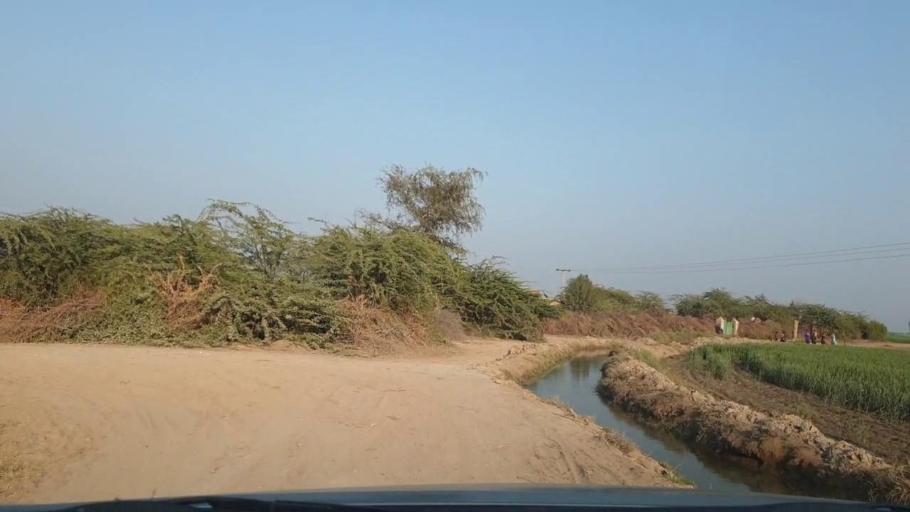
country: PK
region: Sindh
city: Tando Adam
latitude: 25.6868
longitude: 68.6396
